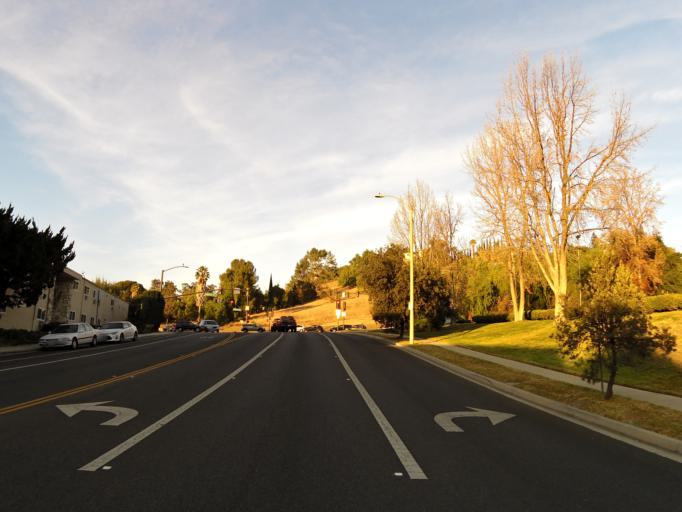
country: US
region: California
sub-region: Ventura County
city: Thousand Oaks
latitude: 34.1816
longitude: -118.8476
